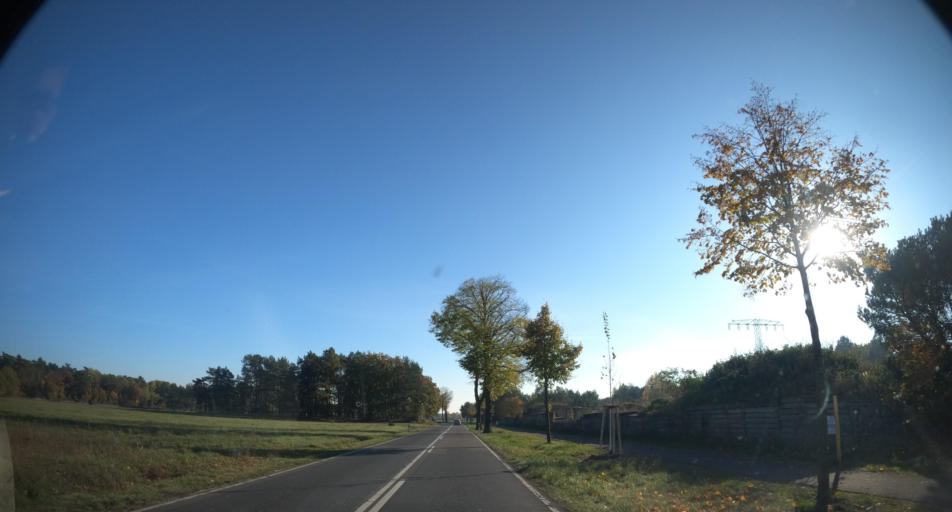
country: DE
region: Mecklenburg-Vorpommern
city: Ueckermunde
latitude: 53.7146
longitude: 14.0657
